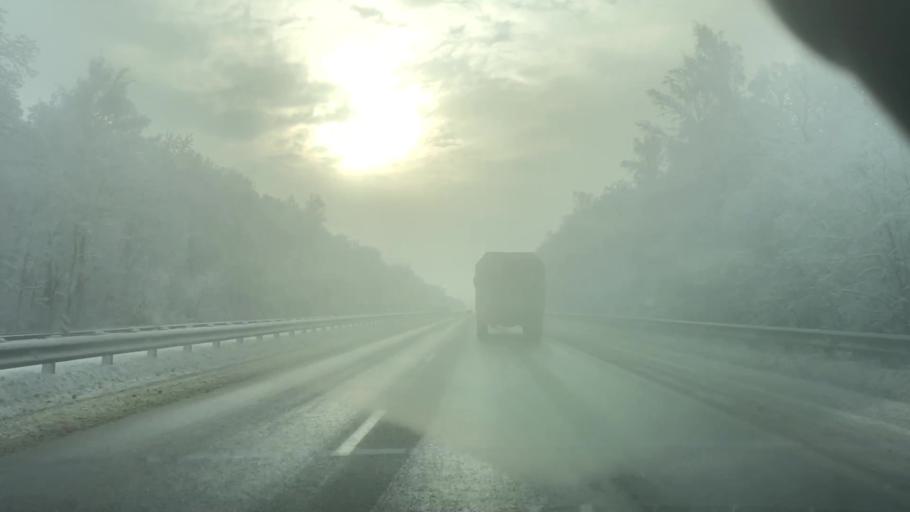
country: RU
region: Tula
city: Venev
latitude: 54.3694
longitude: 38.1547
